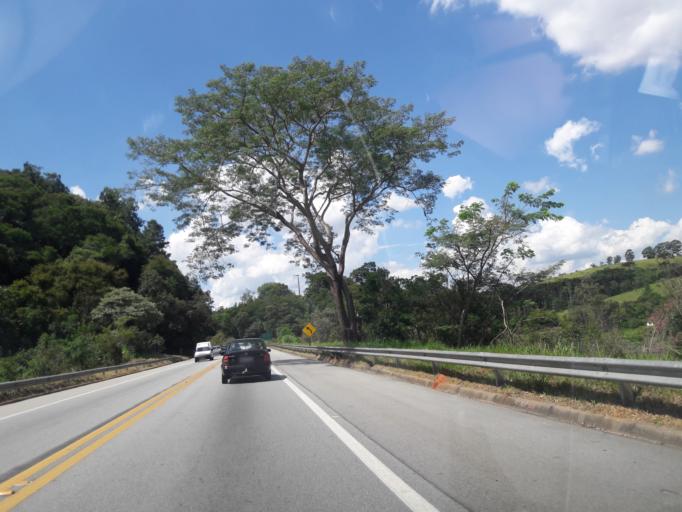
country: BR
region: Sao Paulo
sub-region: Francisco Morato
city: Francisco Morato
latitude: -23.2902
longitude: -46.8025
